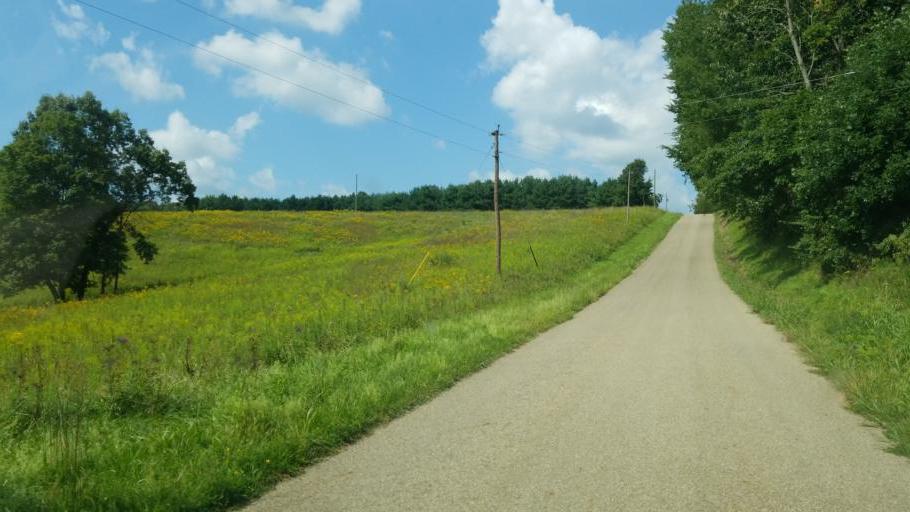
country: US
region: Ohio
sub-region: Knox County
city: Oak Hill
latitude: 40.3896
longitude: -82.3103
